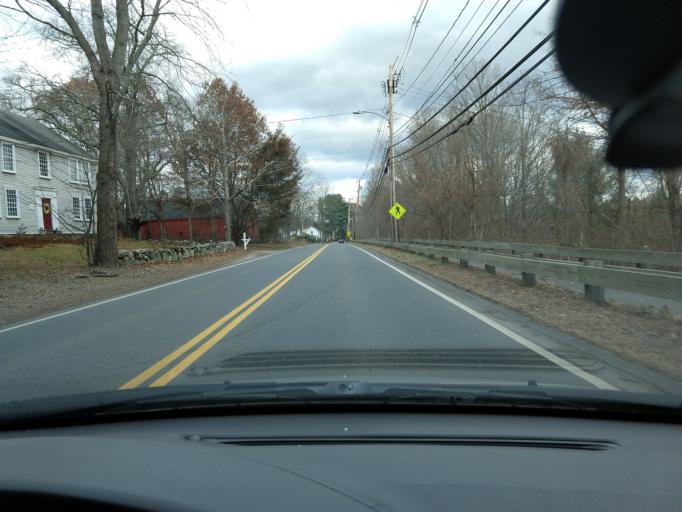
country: US
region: Massachusetts
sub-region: Middlesex County
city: Sudbury
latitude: 42.3991
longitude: -71.4028
